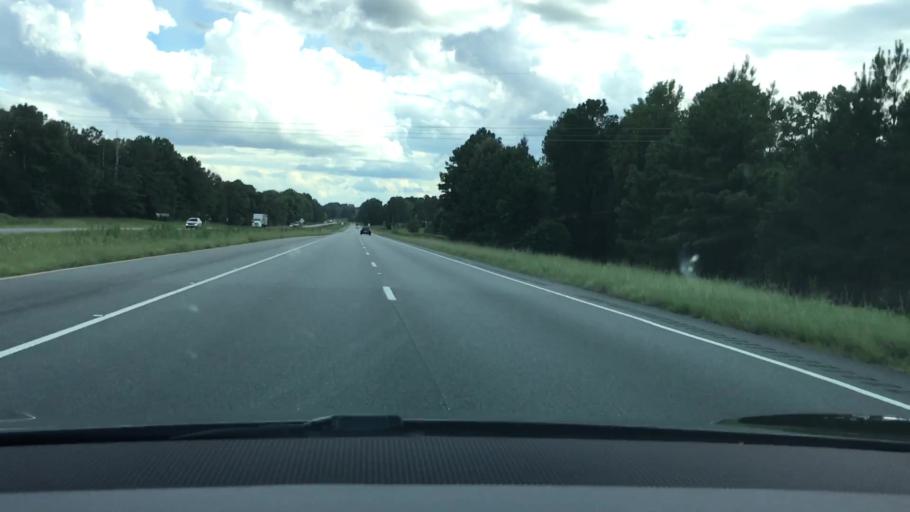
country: US
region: Alabama
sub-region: Pike County
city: Troy
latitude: 31.9597
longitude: -86.0255
